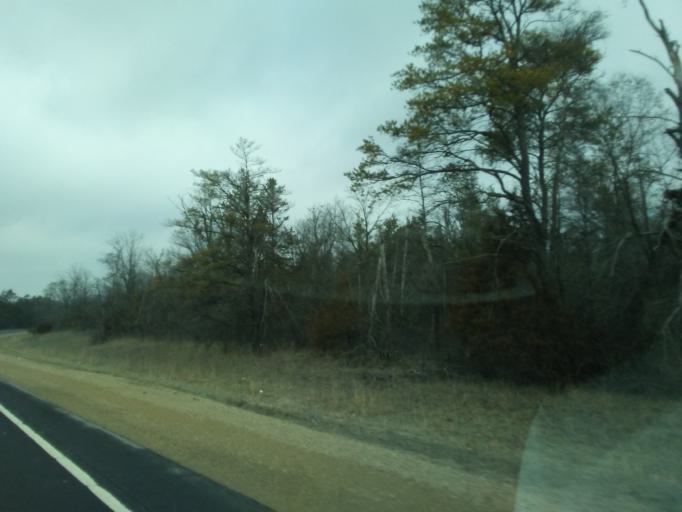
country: US
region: Wisconsin
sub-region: Richland County
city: Richland Center
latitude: 43.2170
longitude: -90.2870
